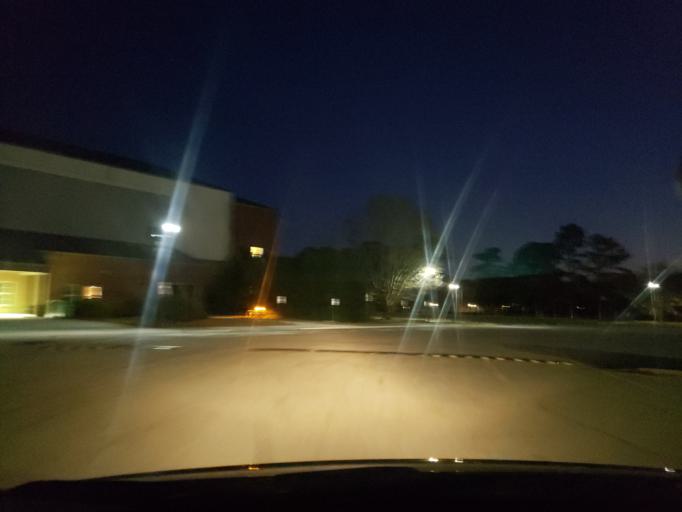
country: US
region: Georgia
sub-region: Chatham County
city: Montgomery
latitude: 31.9774
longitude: -81.1613
